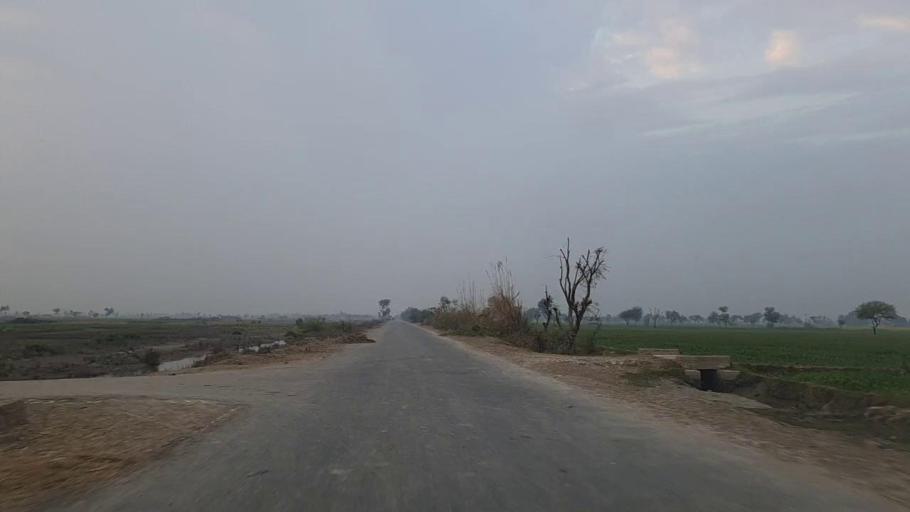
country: PK
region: Sindh
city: Jam Sahib
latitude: 26.3191
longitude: 68.5609
